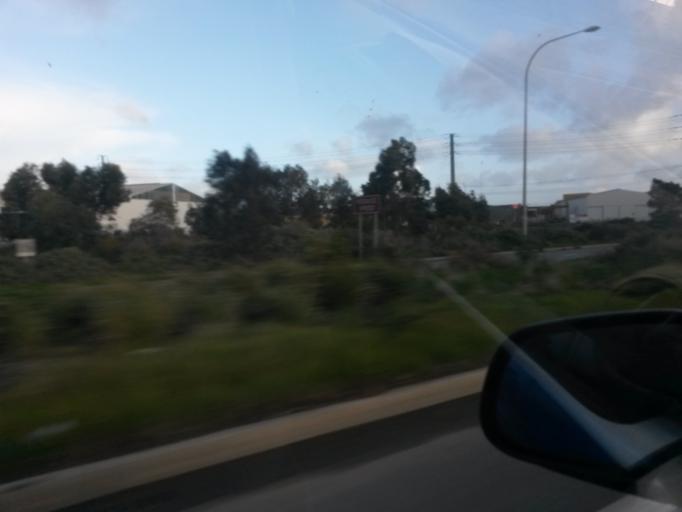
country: AU
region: South Australia
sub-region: Port Adelaide Enfield
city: Alberton
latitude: -34.8378
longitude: 138.5240
